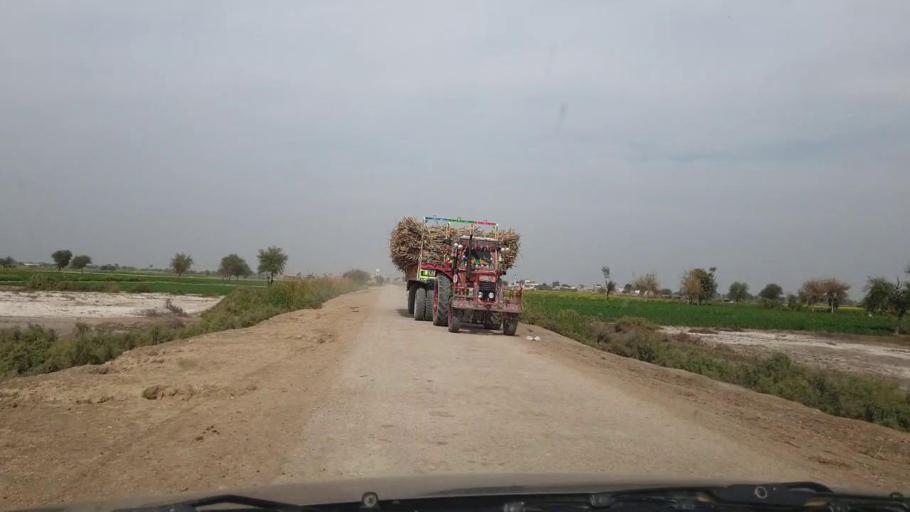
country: PK
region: Sindh
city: Sinjhoro
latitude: 26.0977
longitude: 68.8275
